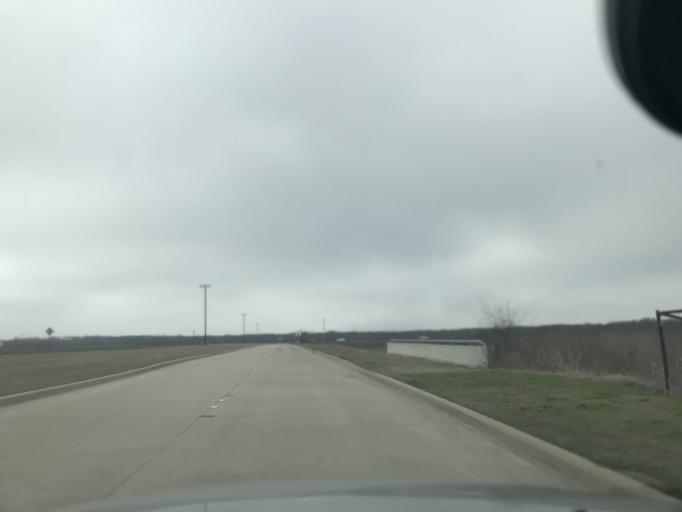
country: US
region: Texas
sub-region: Rockwall County
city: Rockwall
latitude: 32.9797
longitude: -96.4634
